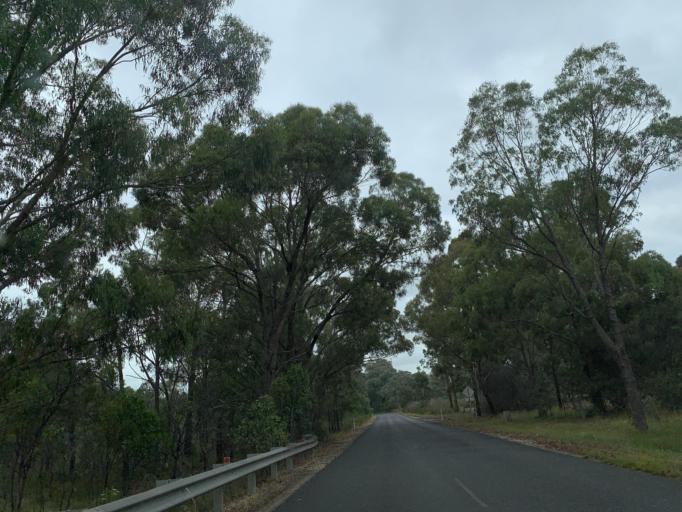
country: AU
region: Victoria
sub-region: Wellington
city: Heyfield
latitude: -37.9330
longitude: 146.7678
